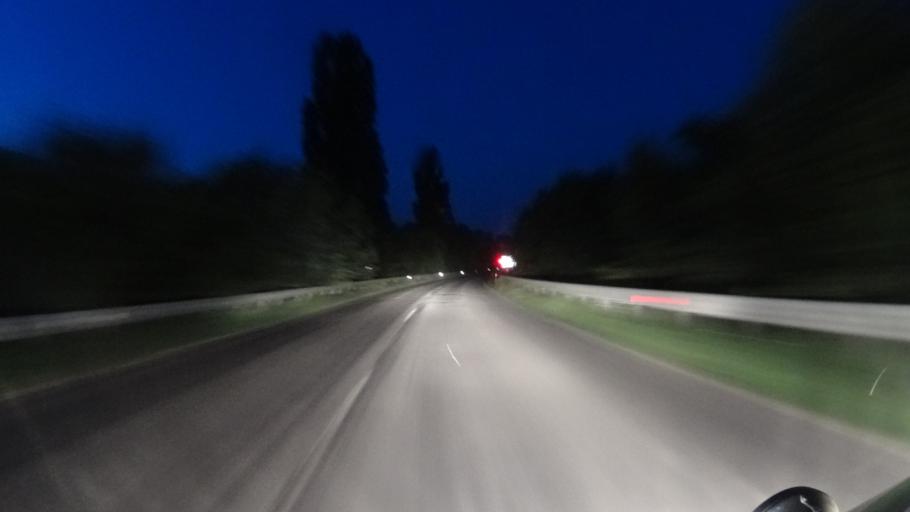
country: HU
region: Somogy
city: Balatonbereny
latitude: 46.6942
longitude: 17.3583
